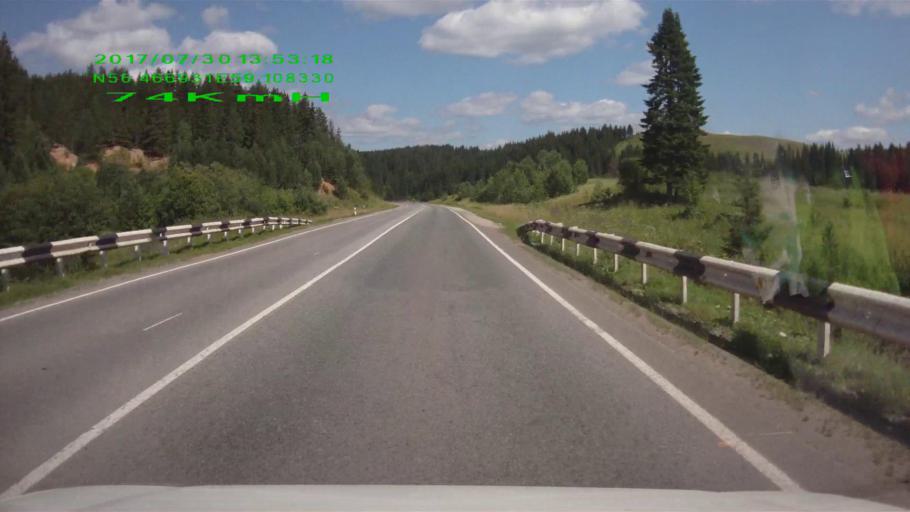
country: RU
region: Sverdlovsk
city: Mikhaylovsk
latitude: 56.4672
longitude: 59.1091
